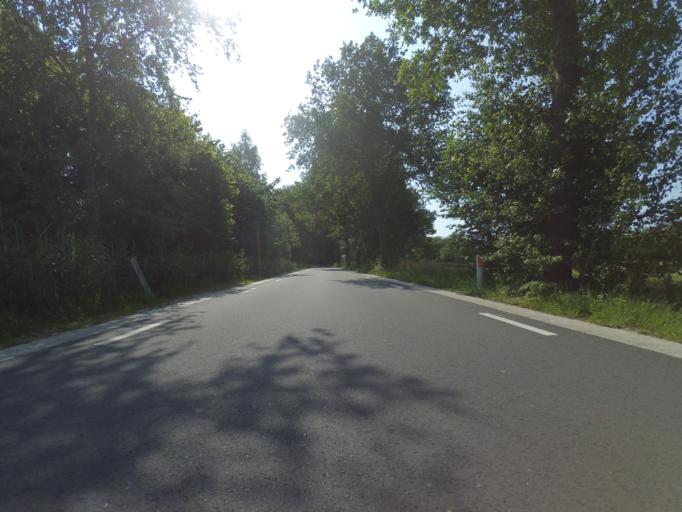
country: NL
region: Gelderland
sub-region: Gemeente Barneveld
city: Terschuur
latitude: 52.1217
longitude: 5.4883
